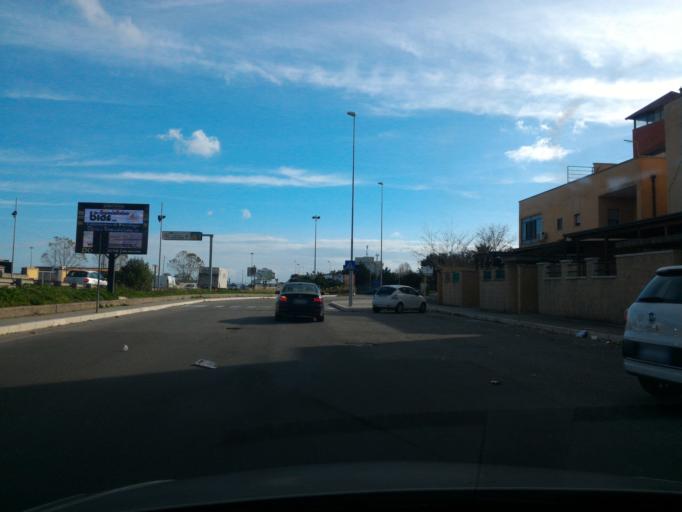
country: IT
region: Calabria
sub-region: Provincia di Crotone
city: Crotone
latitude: 39.0872
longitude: 17.1168
